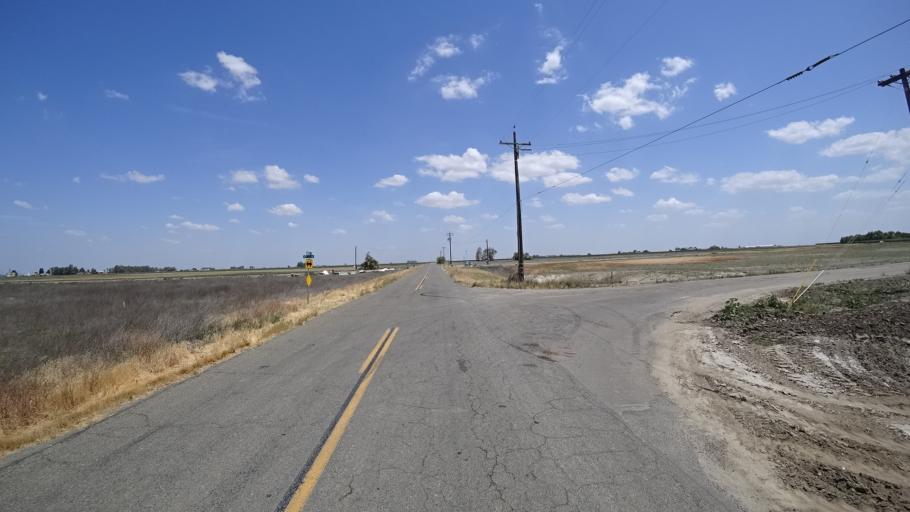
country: US
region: California
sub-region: Kings County
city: Stratford
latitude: 36.1820
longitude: -119.8164
